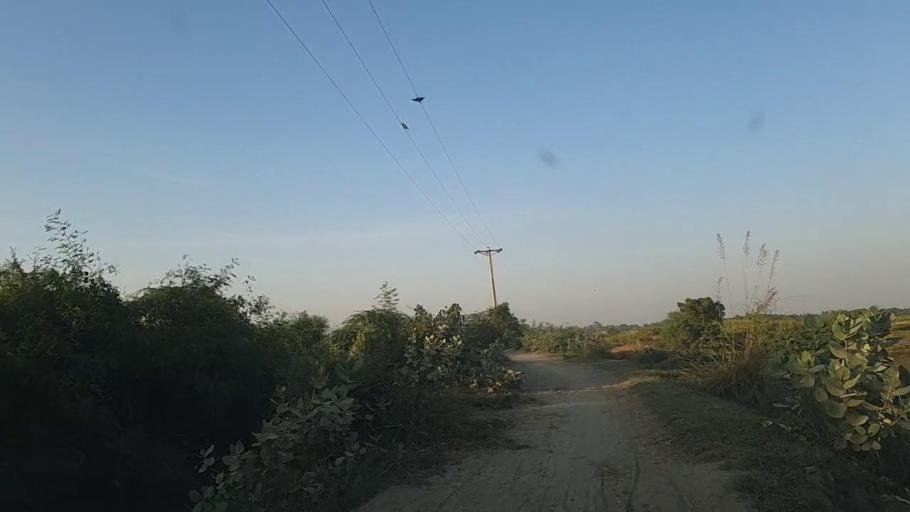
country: PK
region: Sindh
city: Mirpur Batoro
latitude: 24.7249
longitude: 68.2135
